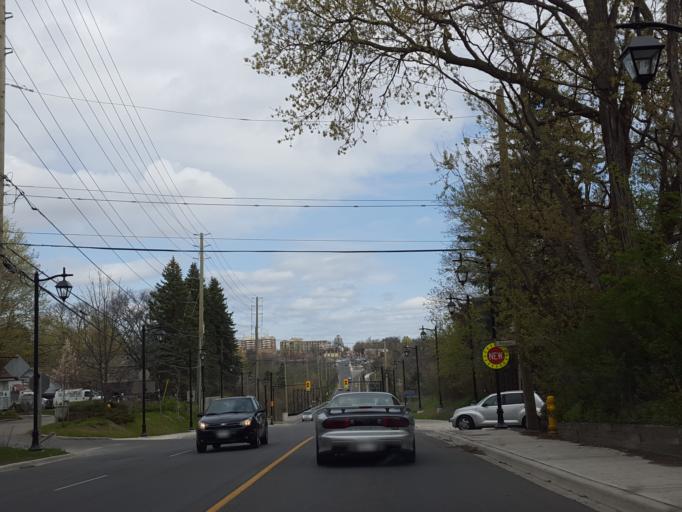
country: CA
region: Ontario
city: Markham
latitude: 43.8669
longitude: -79.2582
